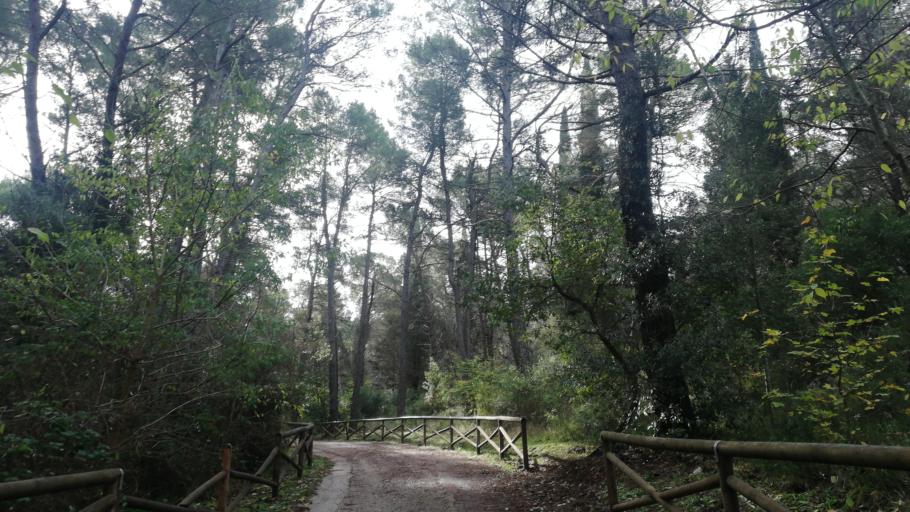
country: IT
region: Apulia
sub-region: Provincia di Bari
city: Cassano delle Murge
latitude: 40.8857
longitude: 16.7023
